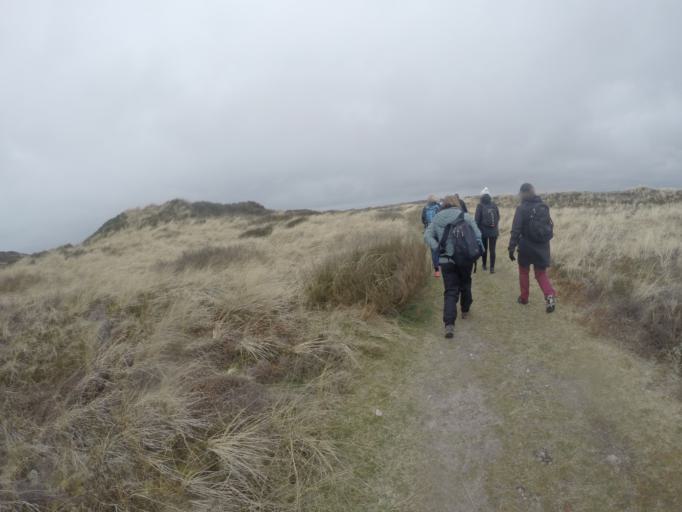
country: DK
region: North Denmark
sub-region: Thisted Kommune
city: Hurup
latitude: 56.8579
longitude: 8.2901
